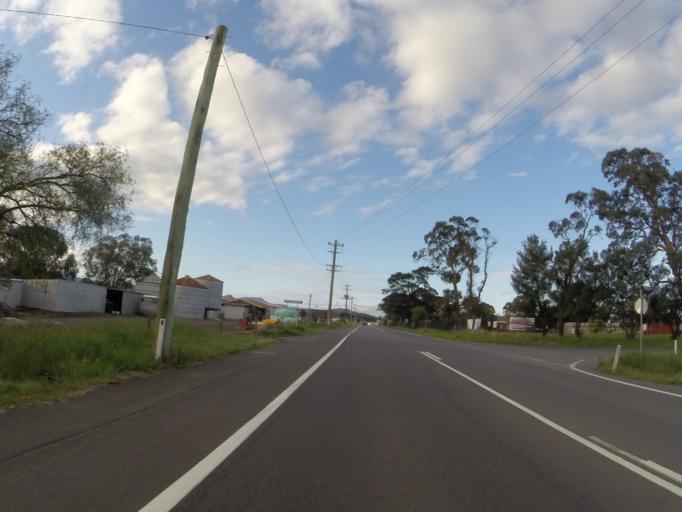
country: AU
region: New South Wales
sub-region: Shellharbour
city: Albion Park Rail
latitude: -34.5529
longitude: 150.7822
